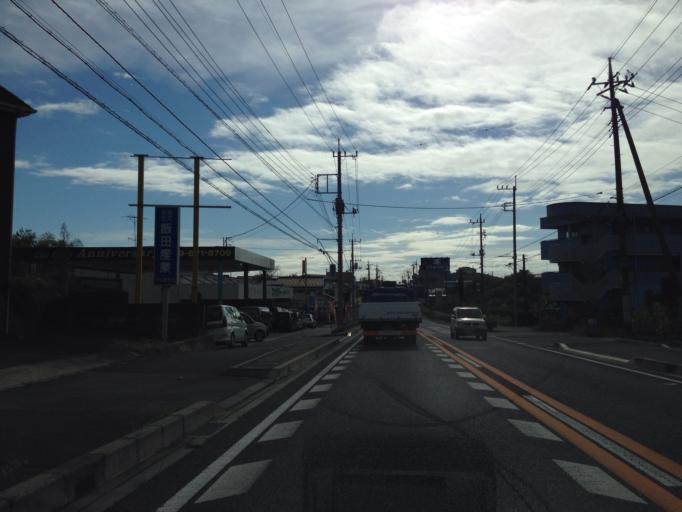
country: JP
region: Ibaraki
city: Ushiku
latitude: 35.9686
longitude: 140.1396
